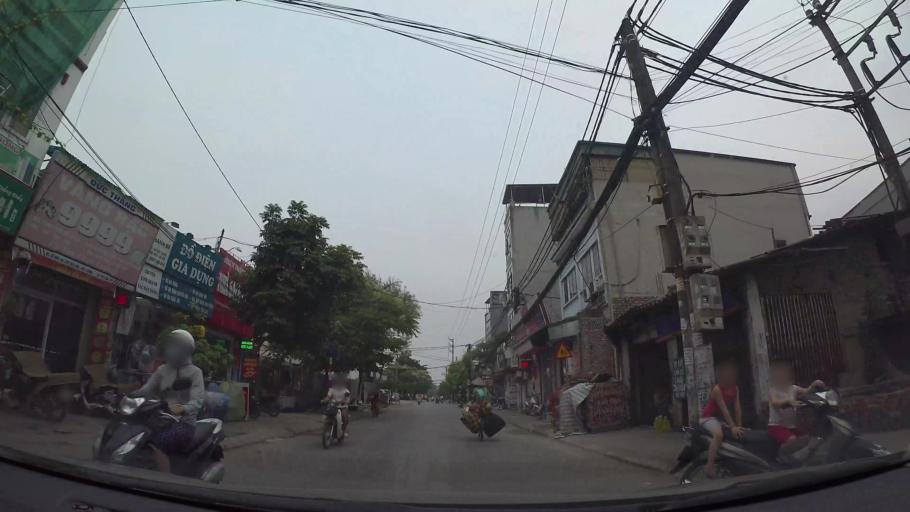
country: VN
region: Ha Noi
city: Hoan Kiem
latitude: 21.0690
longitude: 105.8887
